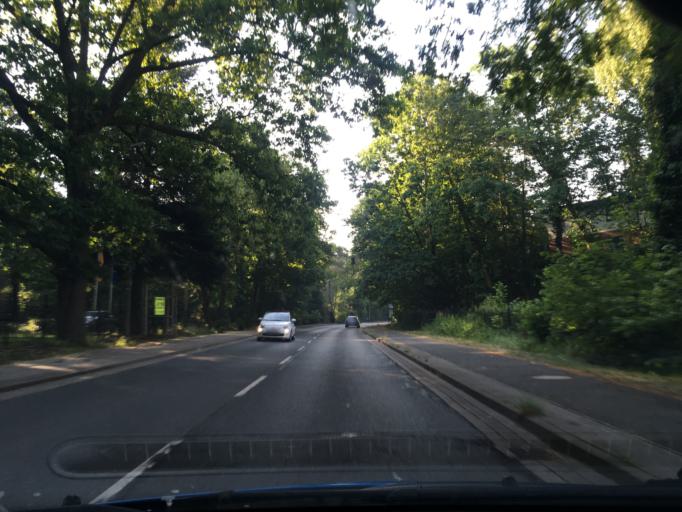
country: DE
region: Lower Saxony
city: Buchholz in der Nordheide
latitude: 53.3372
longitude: 9.8691
